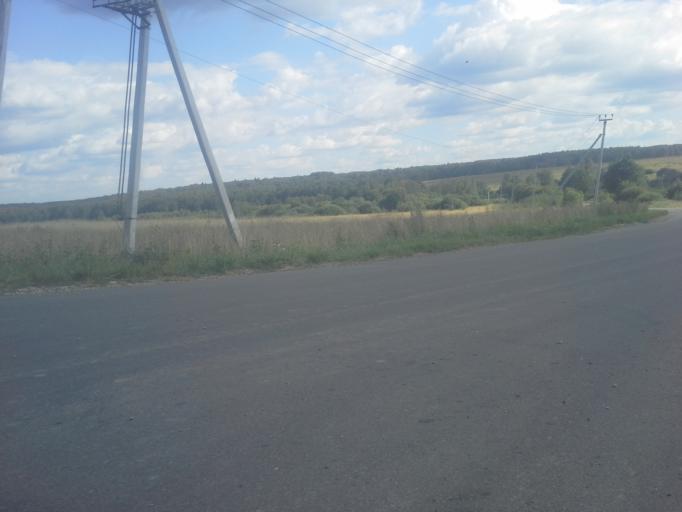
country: RU
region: Moskovskaya
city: Kievskij
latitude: 55.3155
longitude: 37.0268
